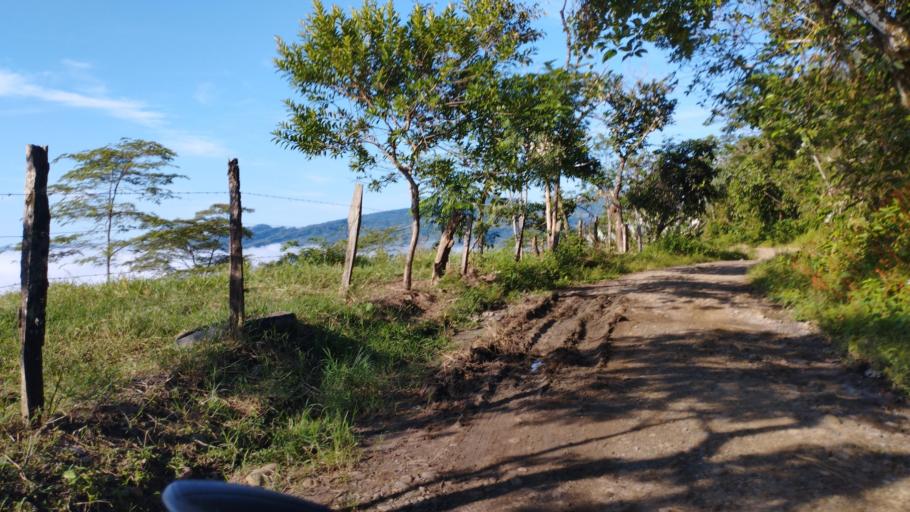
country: CO
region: Casanare
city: Sabanalarga
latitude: 4.7778
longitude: -73.0799
